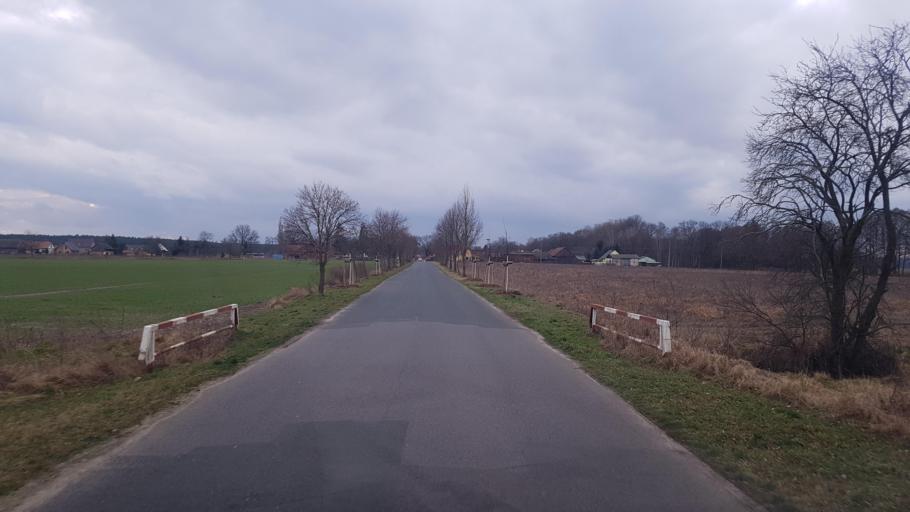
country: DE
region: Brandenburg
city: Kasel-Golzig
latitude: 51.8971
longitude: 13.6480
